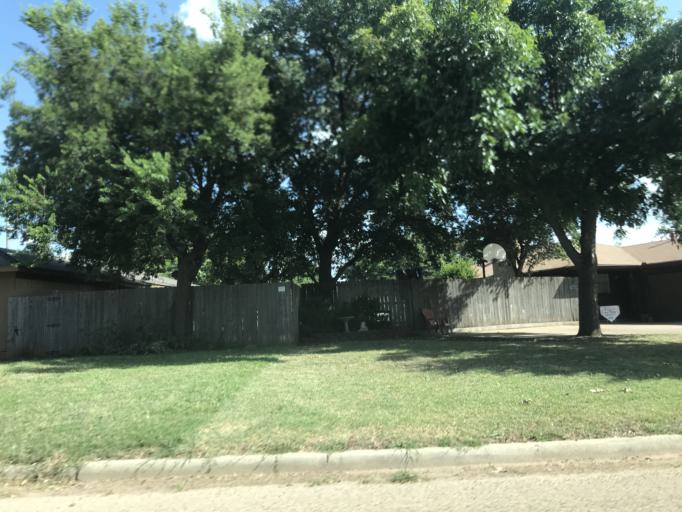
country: US
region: Texas
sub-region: Taylor County
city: Abilene
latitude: 32.4302
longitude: -99.7664
